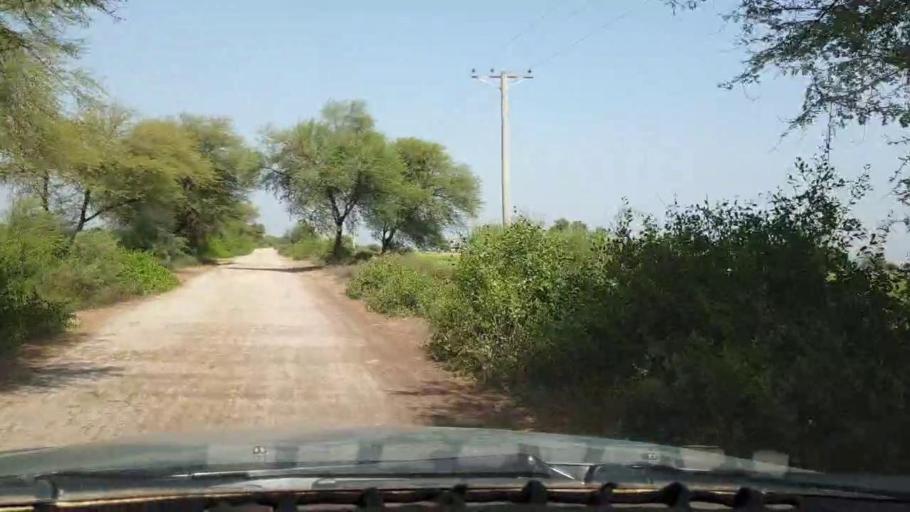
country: PK
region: Sindh
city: Tando Muhammad Khan
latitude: 25.1493
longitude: 68.6338
